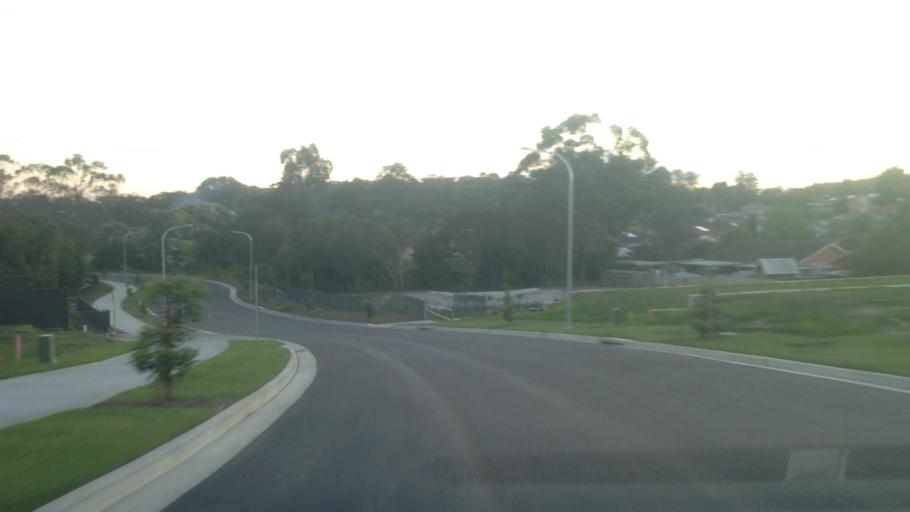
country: AU
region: New South Wales
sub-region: Lake Macquarie Shire
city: Cooranbong
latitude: -33.0714
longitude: 151.4568
